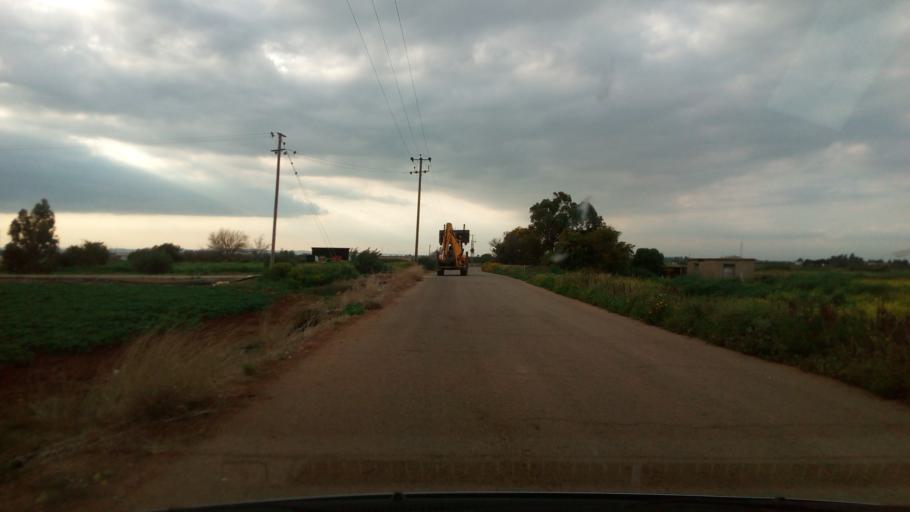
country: CY
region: Ammochostos
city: Avgorou
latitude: 34.9884
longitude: 33.8313
